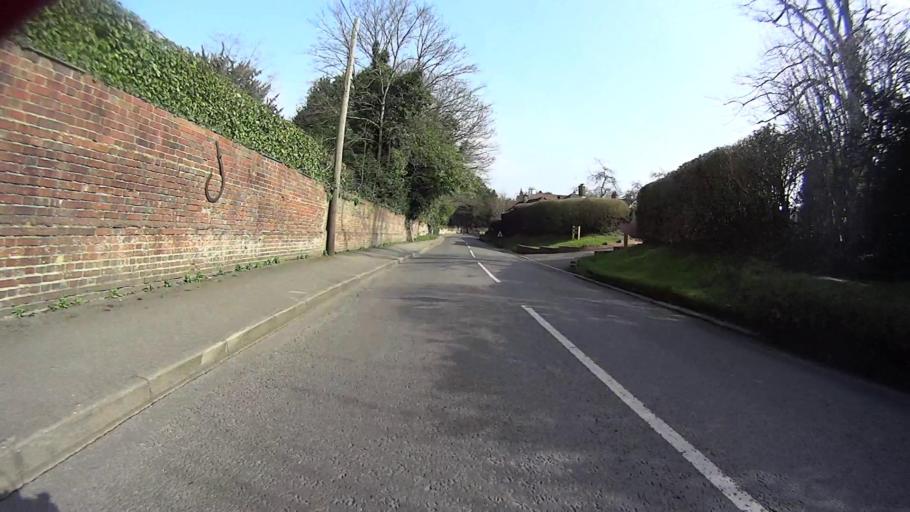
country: GB
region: England
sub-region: Surrey
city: Headley
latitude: 51.2407
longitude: -0.2681
